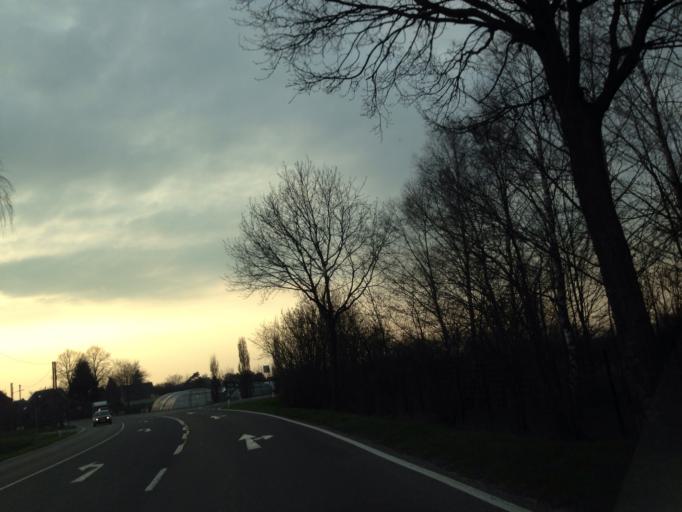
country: DE
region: North Rhine-Westphalia
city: Huckelhoven
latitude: 51.0840
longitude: 6.2582
